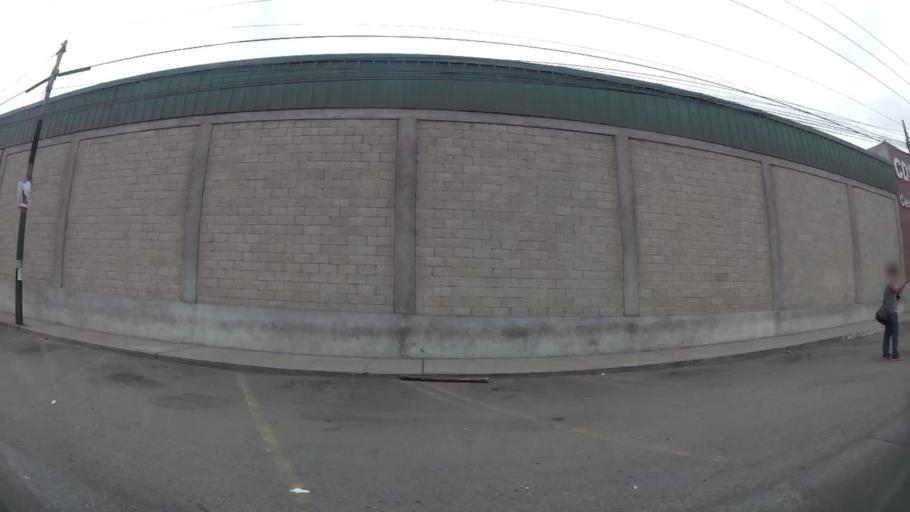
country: PE
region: Callao
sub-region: Callao
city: Callao
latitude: -12.0474
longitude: -77.0879
